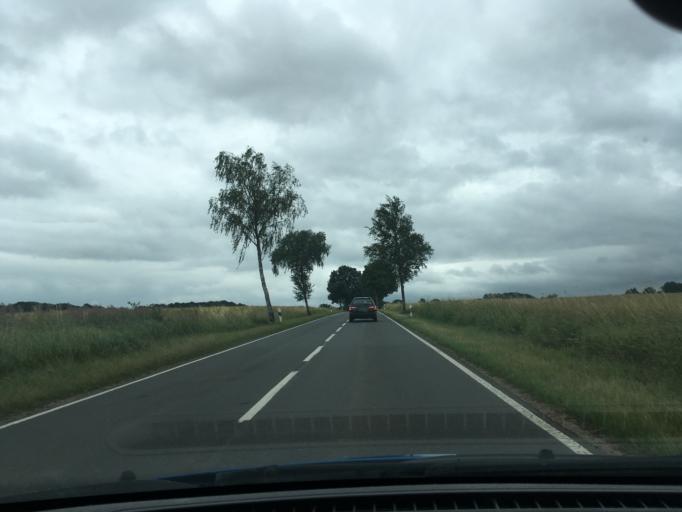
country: DE
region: Lower Saxony
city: Garlstorf
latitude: 53.2453
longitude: 10.1003
